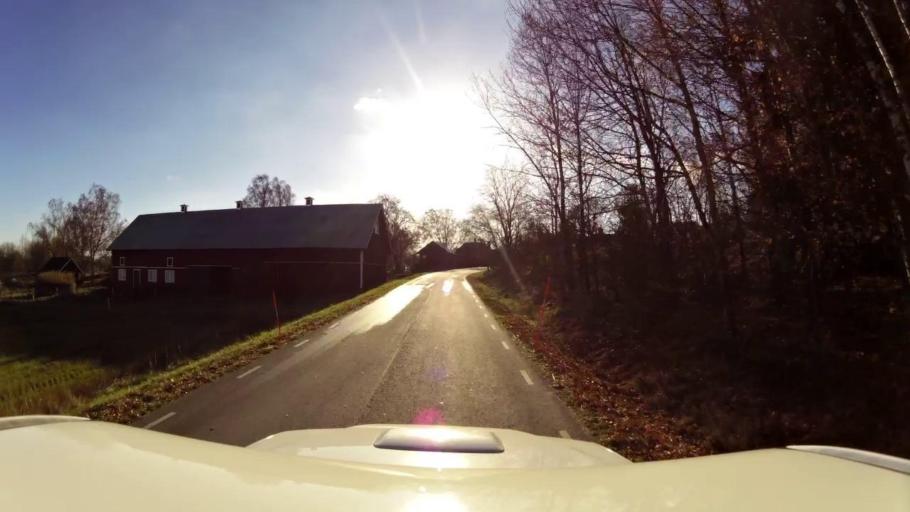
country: SE
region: OEstergoetland
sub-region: Linkopings Kommun
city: Linghem
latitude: 58.4446
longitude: 15.7828
